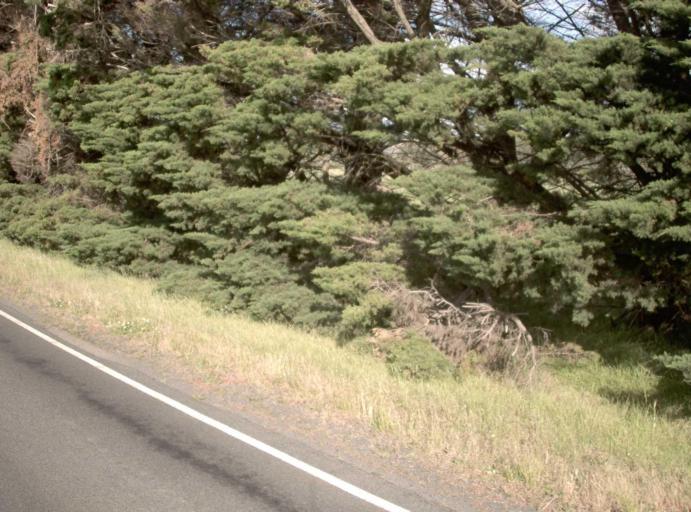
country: AU
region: Victoria
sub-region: Bass Coast
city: North Wonthaggi
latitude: -38.5210
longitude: 145.8926
